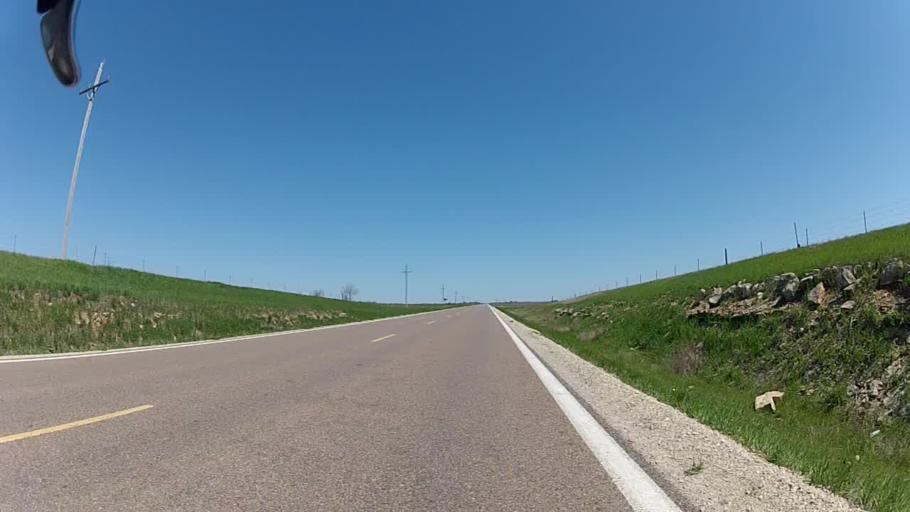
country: US
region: Kansas
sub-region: Wabaunsee County
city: Alma
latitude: 38.9373
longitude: -96.5202
